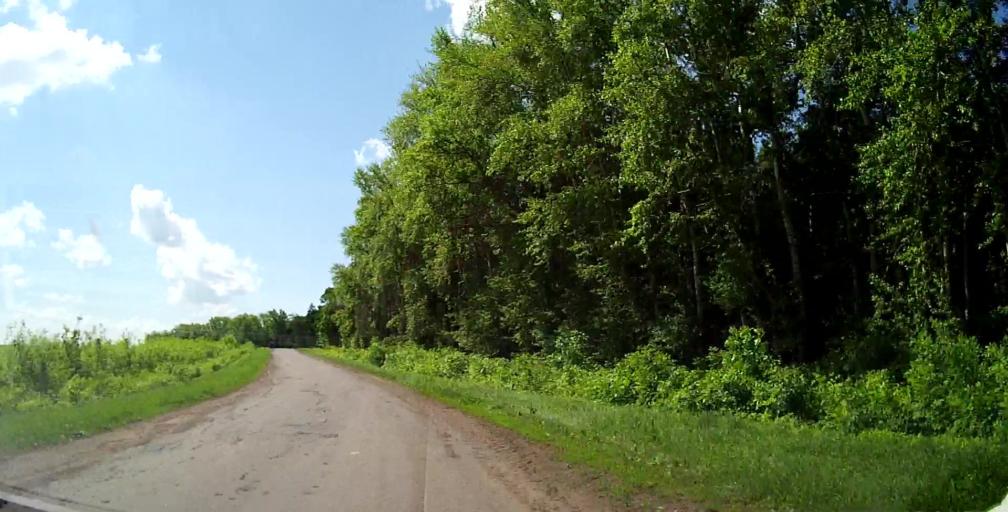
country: RU
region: Lipetsk
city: Chaplygin
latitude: 53.3030
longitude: 39.9518
